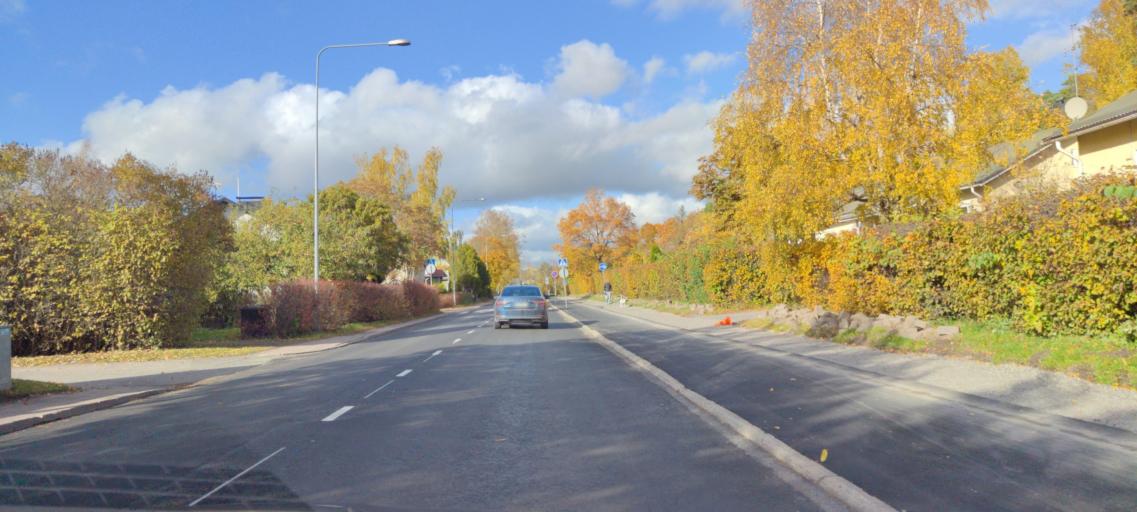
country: FI
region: Varsinais-Suomi
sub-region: Turku
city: Turku
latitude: 60.4341
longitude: 22.2648
